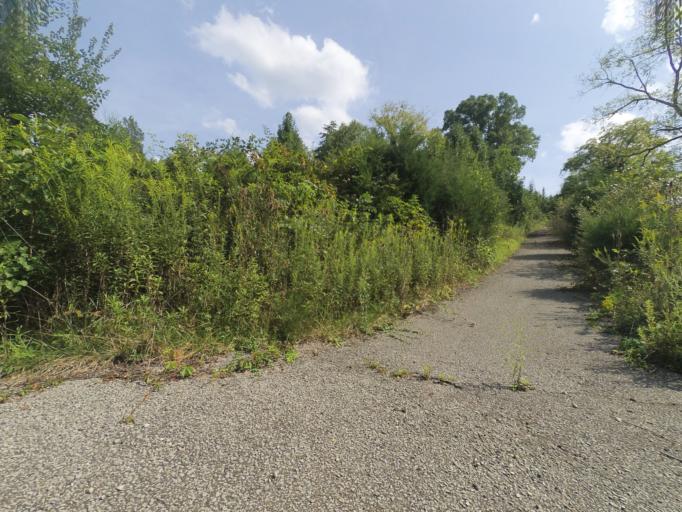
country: US
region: Ohio
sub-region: Lawrence County
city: Burlington
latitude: 38.3849
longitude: -82.5108
